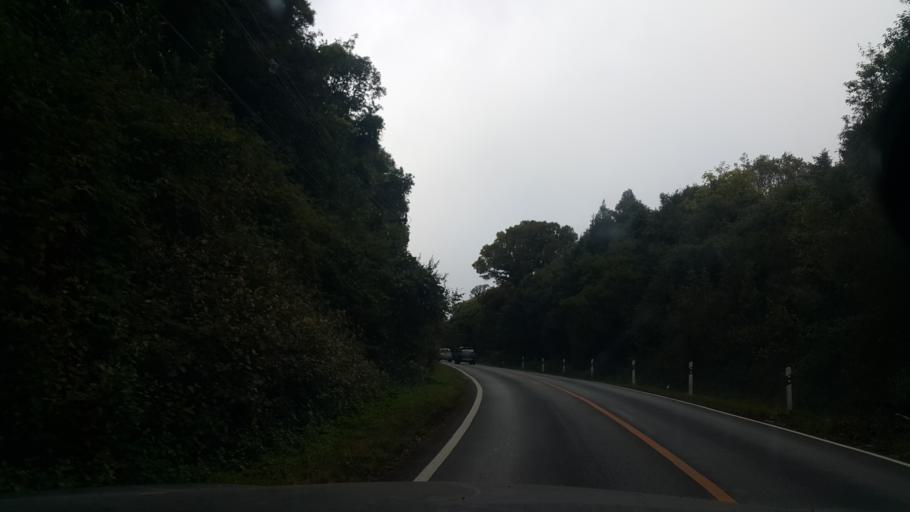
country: TH
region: Chiang Mai
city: Mae Chaem
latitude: 18.5778
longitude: 98.4826
